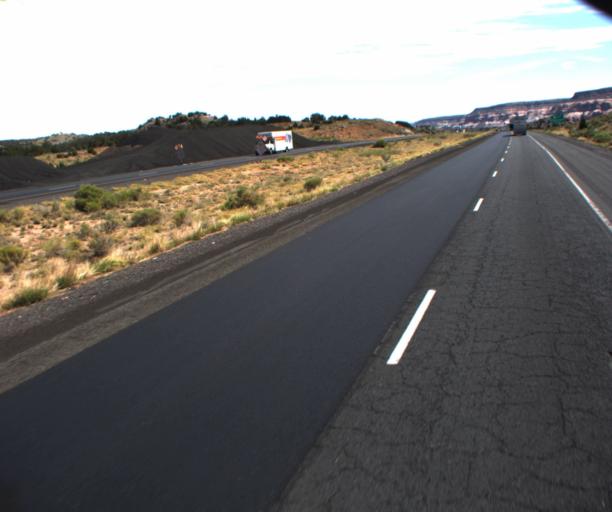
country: US
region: Arizona
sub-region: Apache County
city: Houck
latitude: 35.3159
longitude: -109.0953
